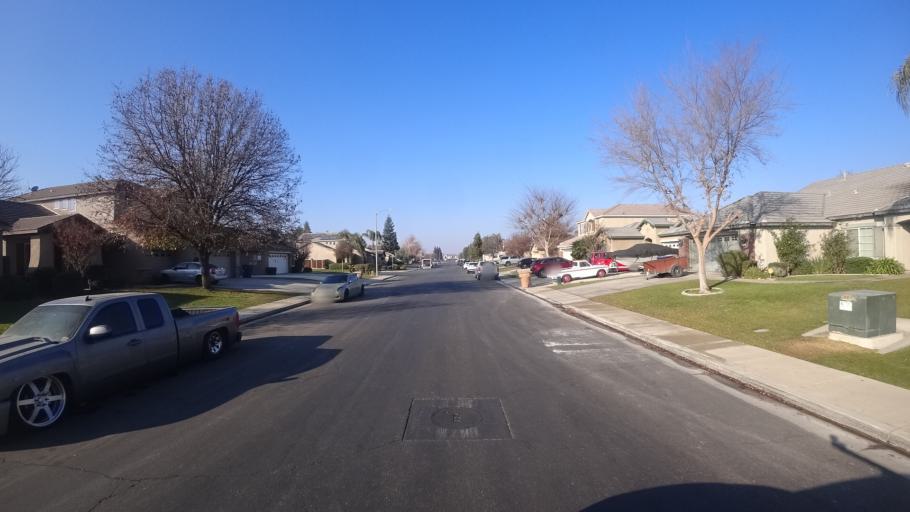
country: US
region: California
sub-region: Kern County
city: Greenacres
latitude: 35.3040
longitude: -119.1200
